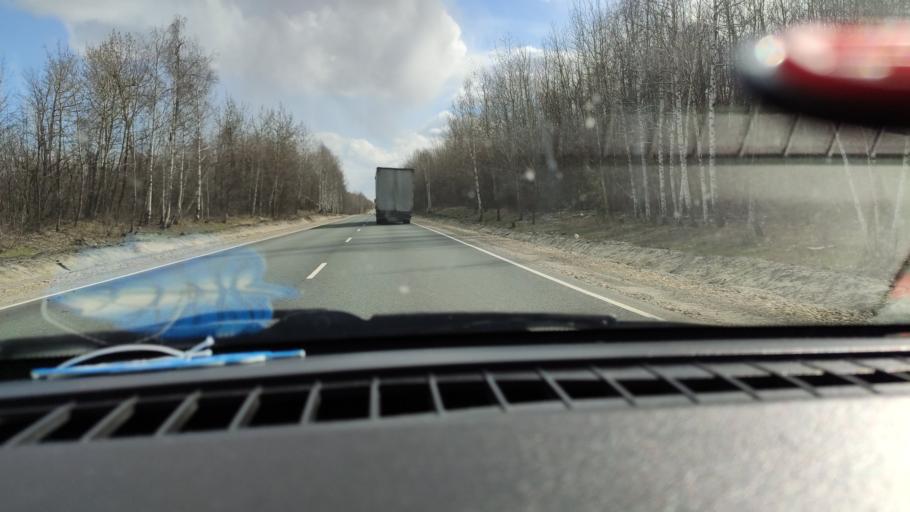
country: RU
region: Saratov
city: Khvalynsk
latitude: 52.4309
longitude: 48.0088
